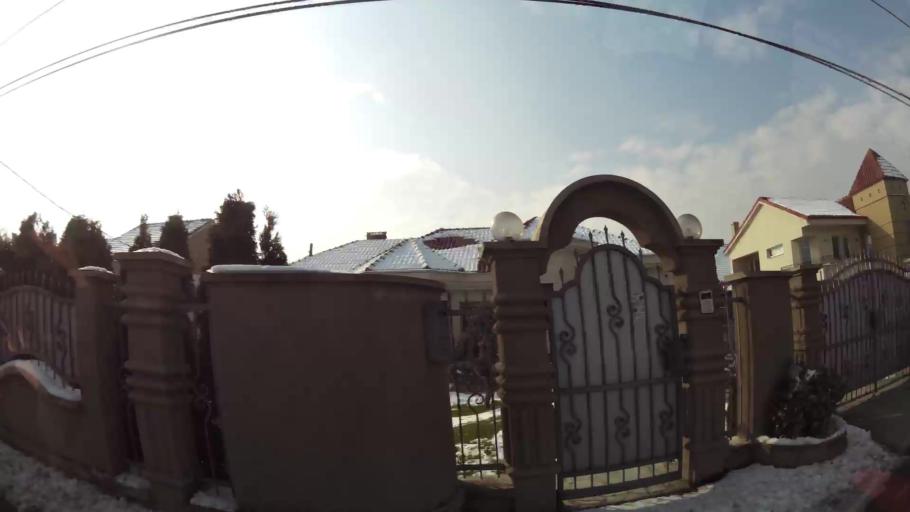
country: MK
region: Suto Orizari
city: Suto Orizare
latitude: 42.0140
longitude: 21.3894
